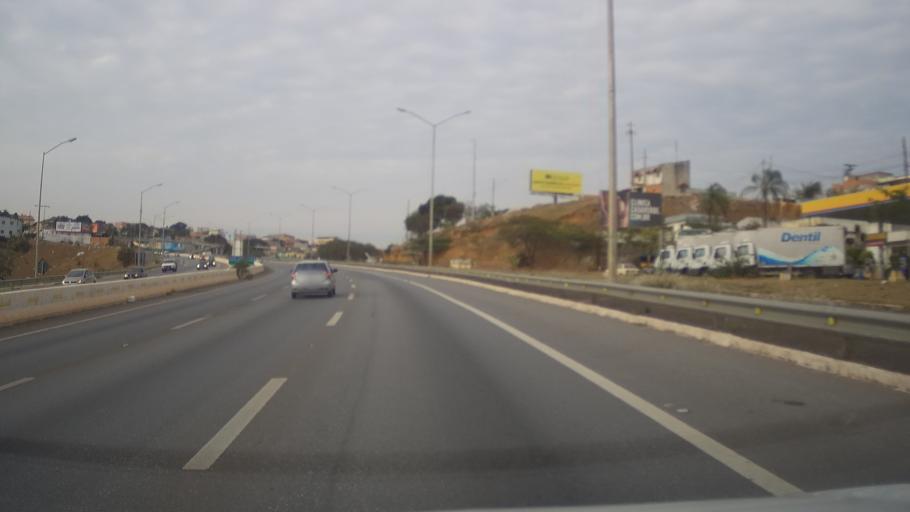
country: BR
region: Minas Gerais
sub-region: Vespasiano
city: Vespasiano
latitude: -19.7431
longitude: -43.9505
